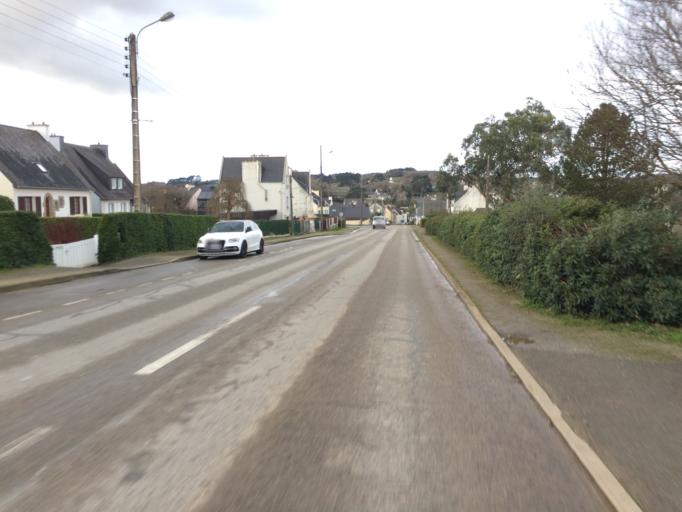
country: FR
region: Brittany
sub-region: Departement du Finistere
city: Daoulas
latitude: 48.3558
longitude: -4.2573
